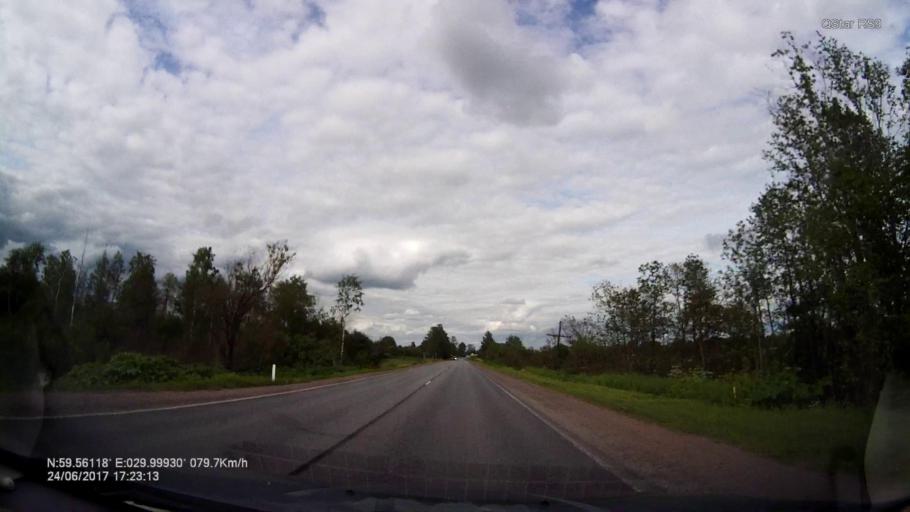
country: RU
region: Leningrad
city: Voyskovitsy
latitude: 59.5614
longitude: 29.9999
